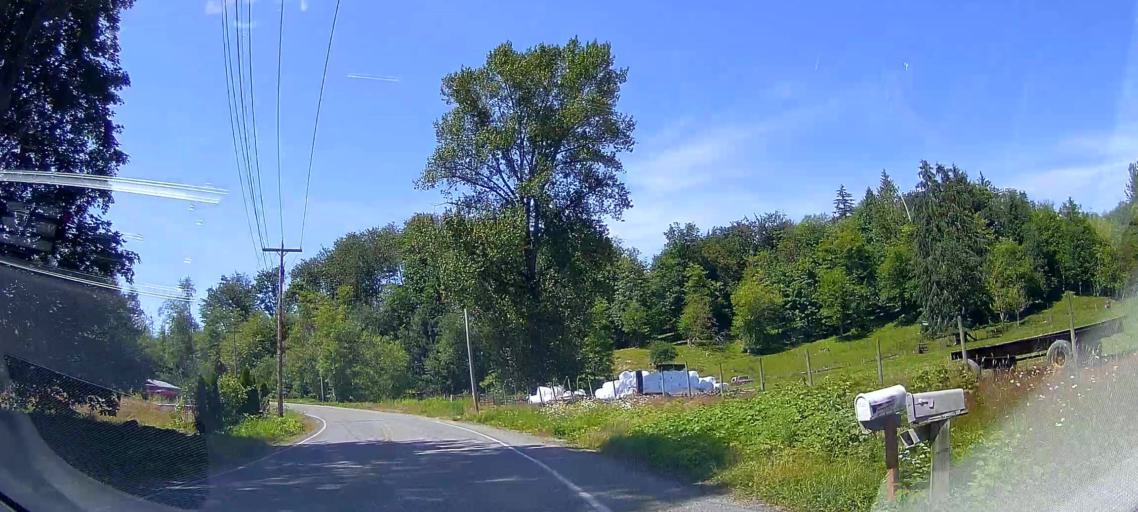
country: US
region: Washington
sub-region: Skagit County
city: Sedro-Woolley
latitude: 48.5835
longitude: -122.2876
